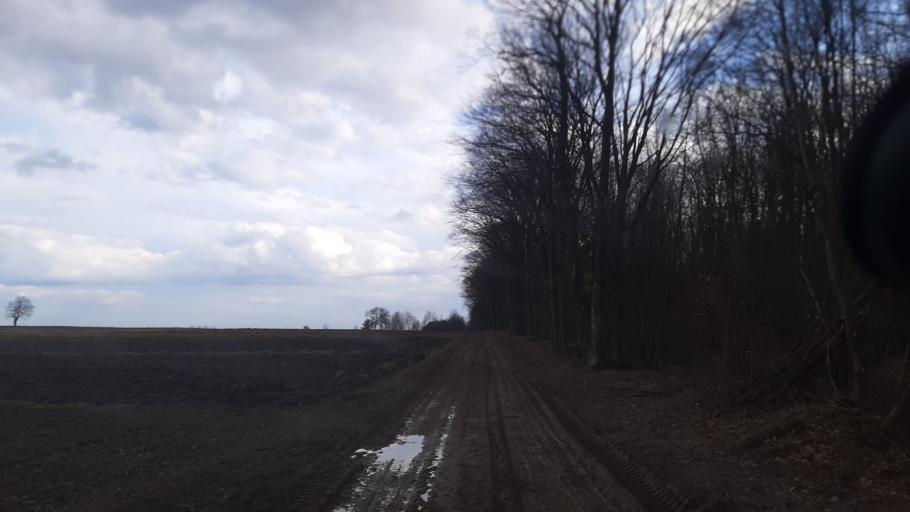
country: PL
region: Lublin Voivodeship
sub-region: Powiat lubelski
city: Jastkow
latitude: 51.3744
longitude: 22.4145
